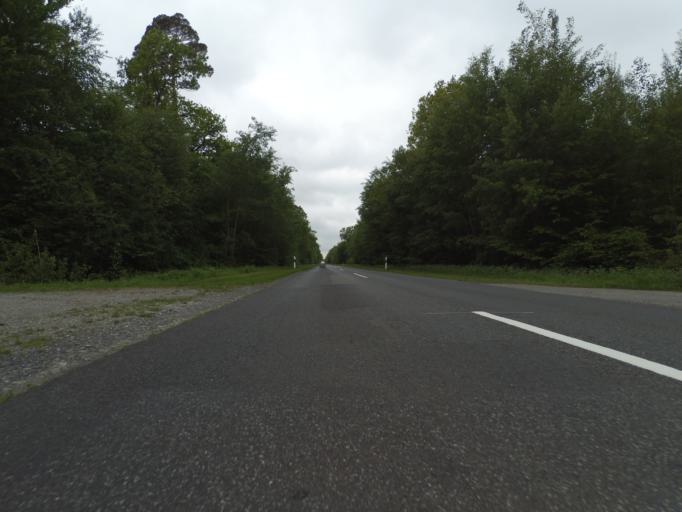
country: DE
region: Lower Saxony
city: Ribbesbuttel
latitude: 52.4074
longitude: 10.4979
